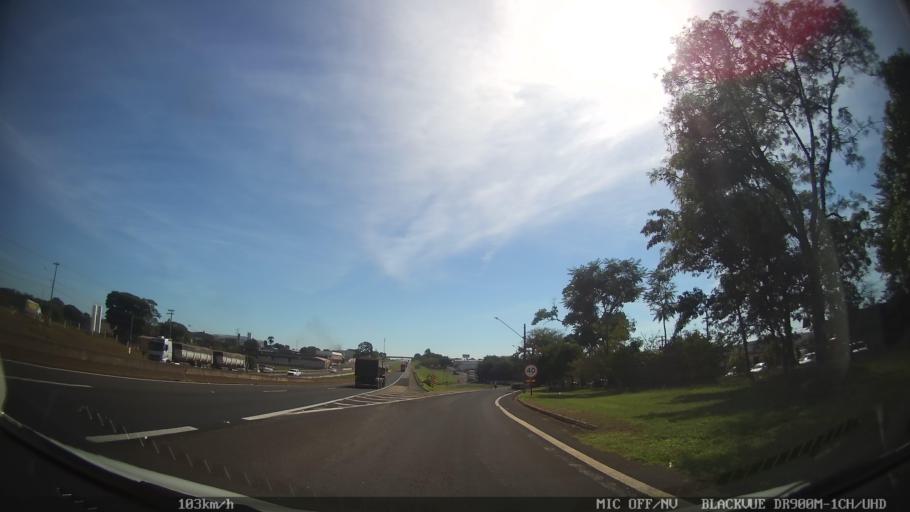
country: BR
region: Sao Paulo
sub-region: Porto Ferreira
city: Porto Ferreira
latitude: -21.8681
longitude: -47.4900
